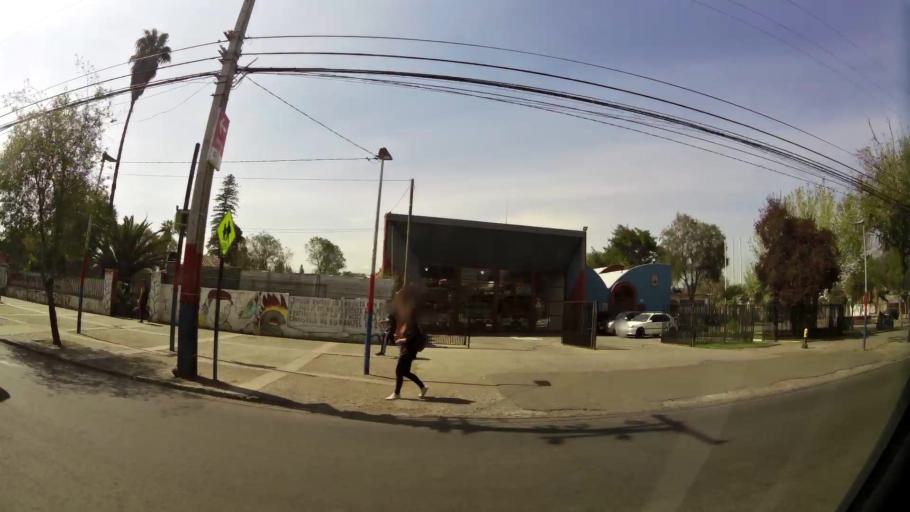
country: CL
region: Santiago Metropolitan
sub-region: Provincia de Santiago
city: Lo Prado
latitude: -33.4378
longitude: -70.7524
